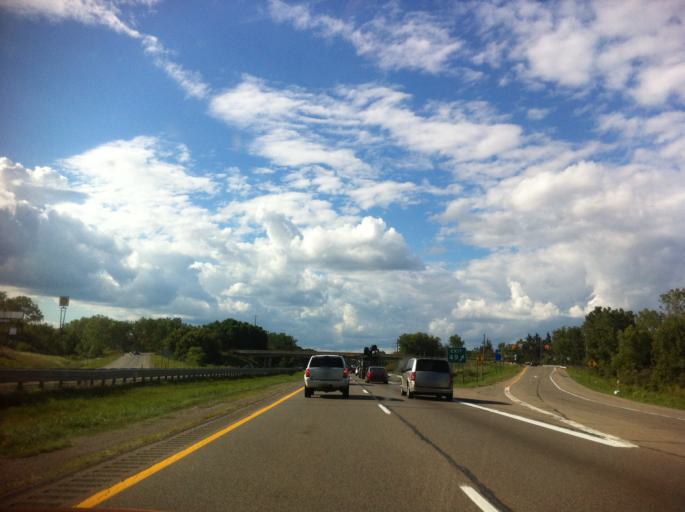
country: US
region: Michigan
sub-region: Livingston County
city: Whitmore Lake
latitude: 42.3774
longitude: -83.7555
